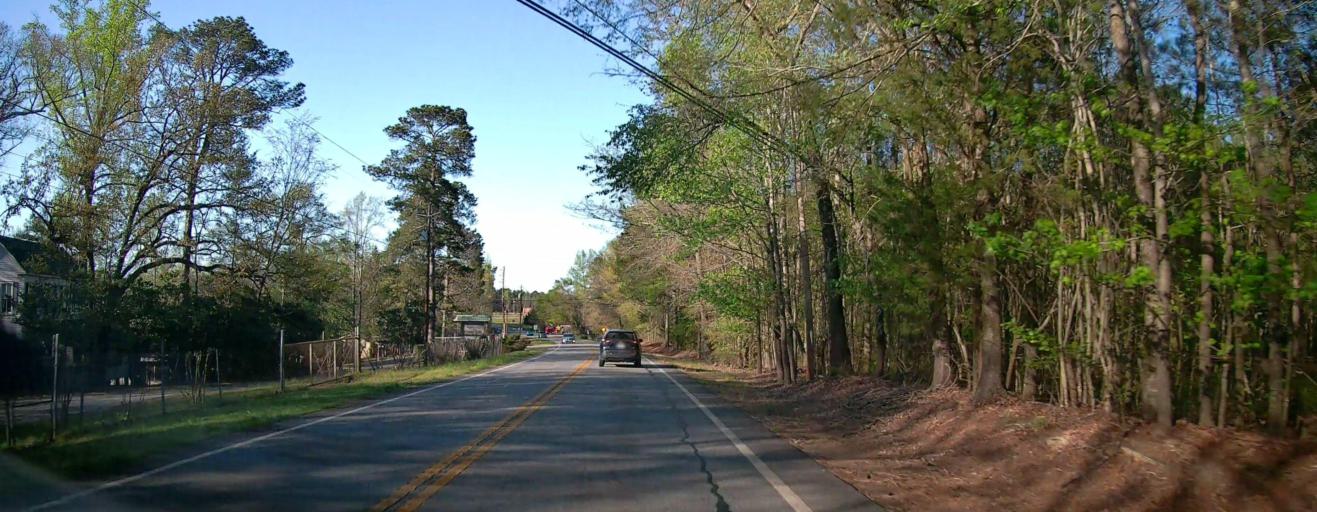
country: US
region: Georgia
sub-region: Butts County
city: Indian Springs
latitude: 33.2595
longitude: -83.9097
